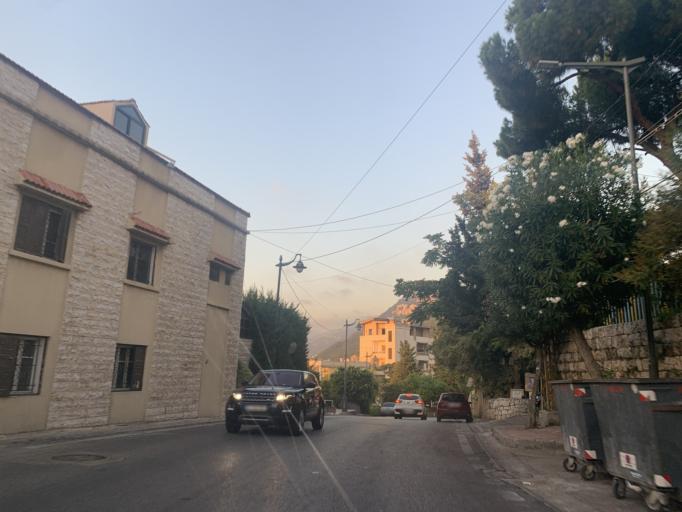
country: LB
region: Mont-Liban
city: Djounie
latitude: 33.9657
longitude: 35.6257
